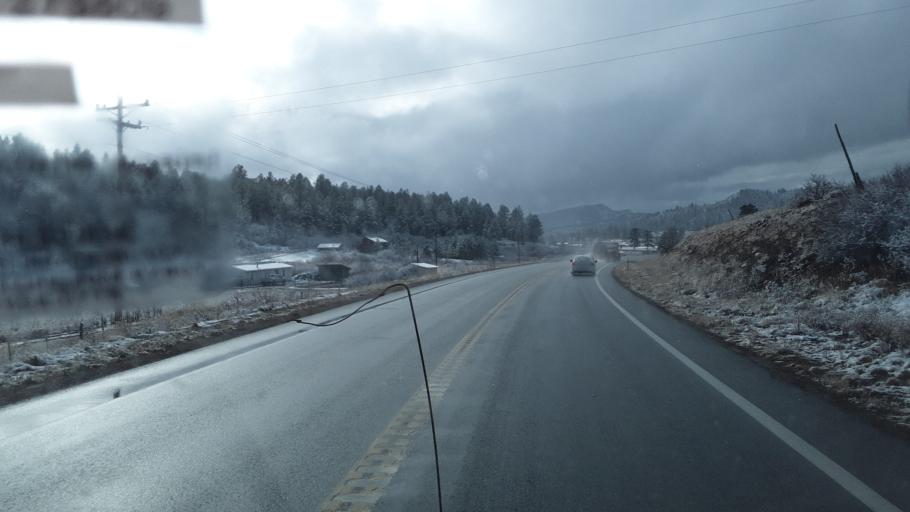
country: US
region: Colorado
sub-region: Archuleta County
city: Pagosa Springs
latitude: 37.2371
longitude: -107.1683
